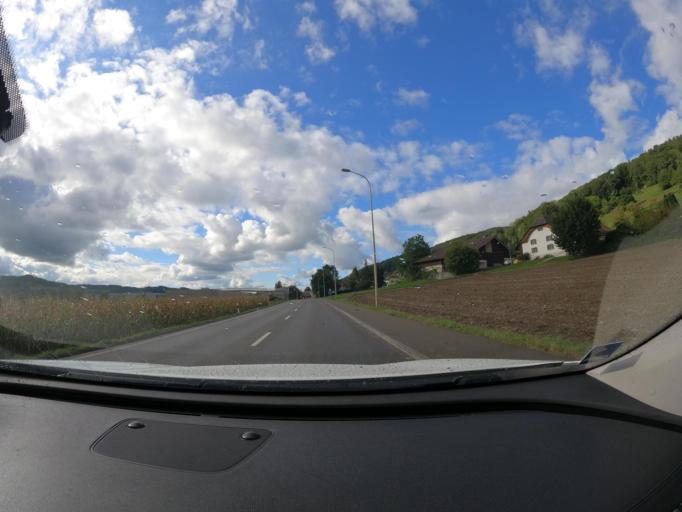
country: CH
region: Aargau
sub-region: Bezirk Kulm
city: Reinach
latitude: 47.2689
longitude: 8.1745
